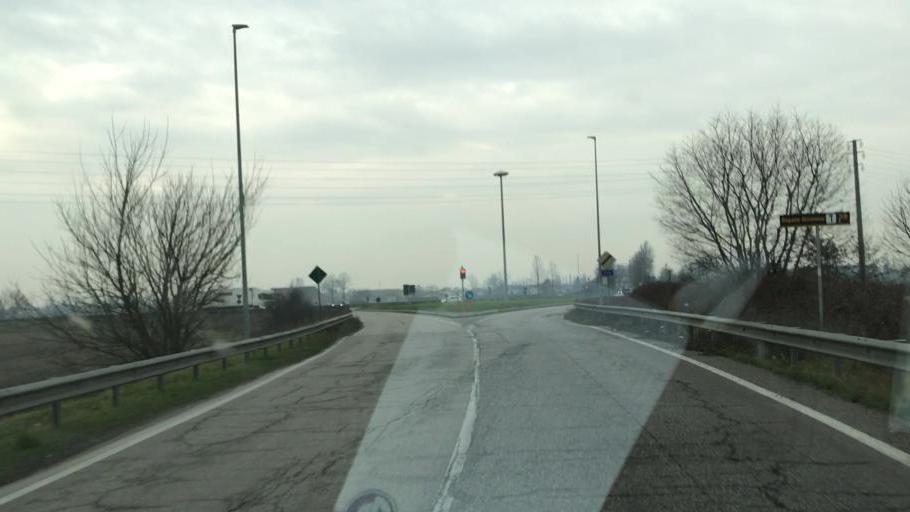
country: IT
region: Lombardy
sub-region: Provincia di Mantova
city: Asola
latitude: 45.2311
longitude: 10.4169
